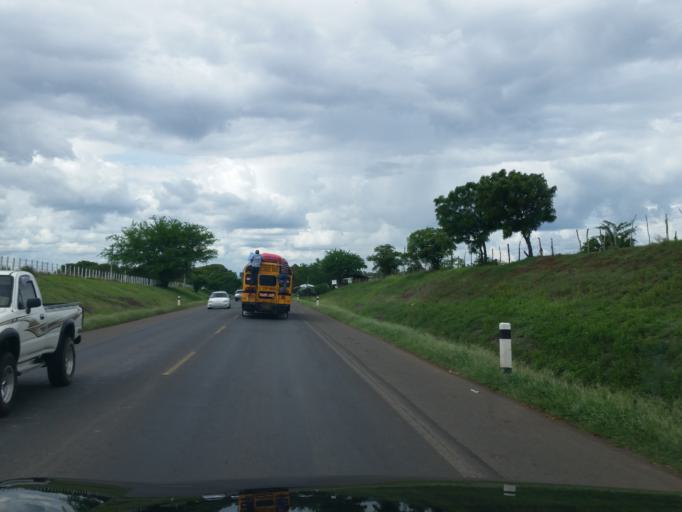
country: NI
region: Managua
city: Tipitapa
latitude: 12.2343
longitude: -86.0928
